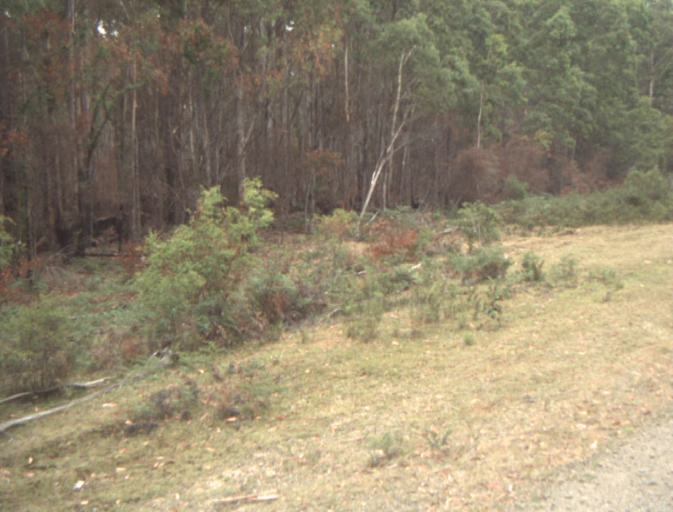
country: AU
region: Tasmania
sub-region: Dorset
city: Scottsdale
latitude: -41.4350
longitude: 147.5150
